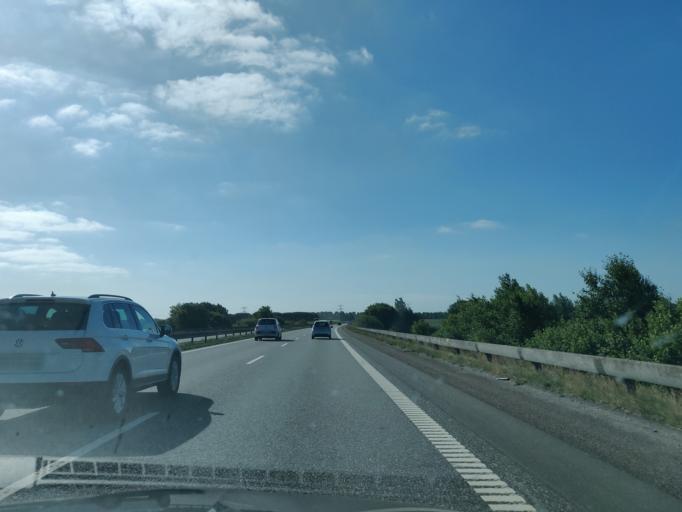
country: DK
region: Central Jutland
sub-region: Randers Kommune
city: Spentrup
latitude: 56.5181
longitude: 9.9596
